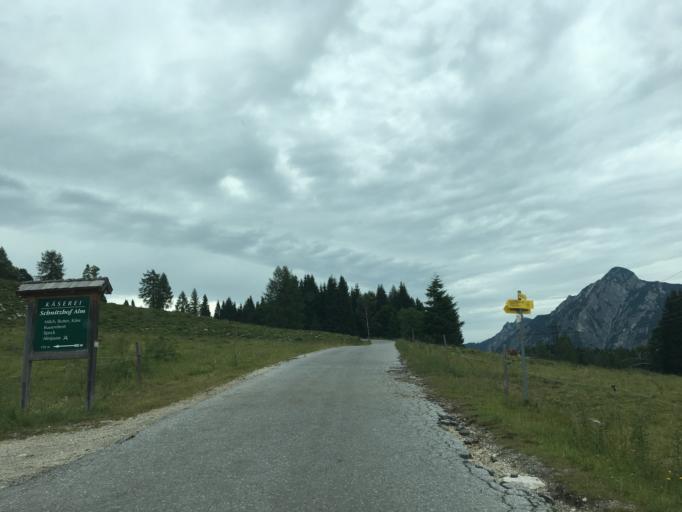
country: AT
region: Salzburg
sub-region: Politischer Bezirk Salzburg-Umgebung
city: Strobl
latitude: 47.6535
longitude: 13.4356
